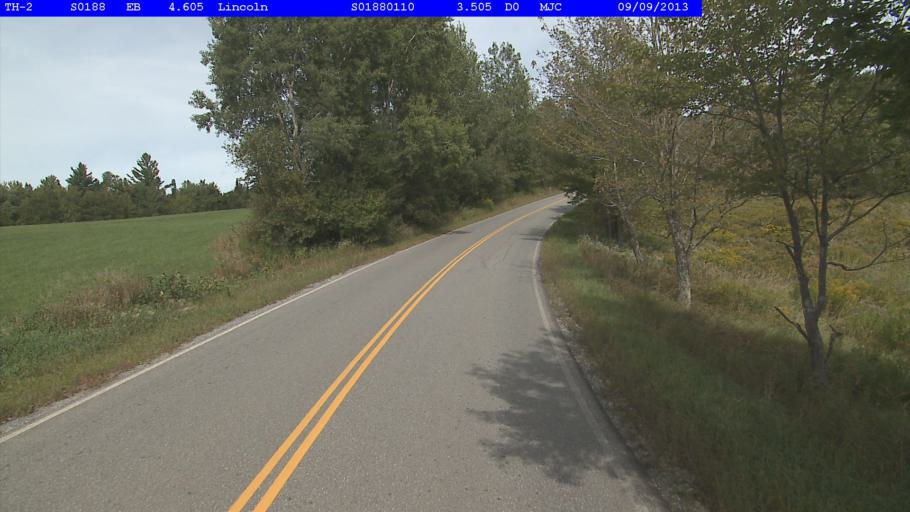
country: US
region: Vermont
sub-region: Addison County
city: Bristol
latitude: 44.0966
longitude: -72.9803
